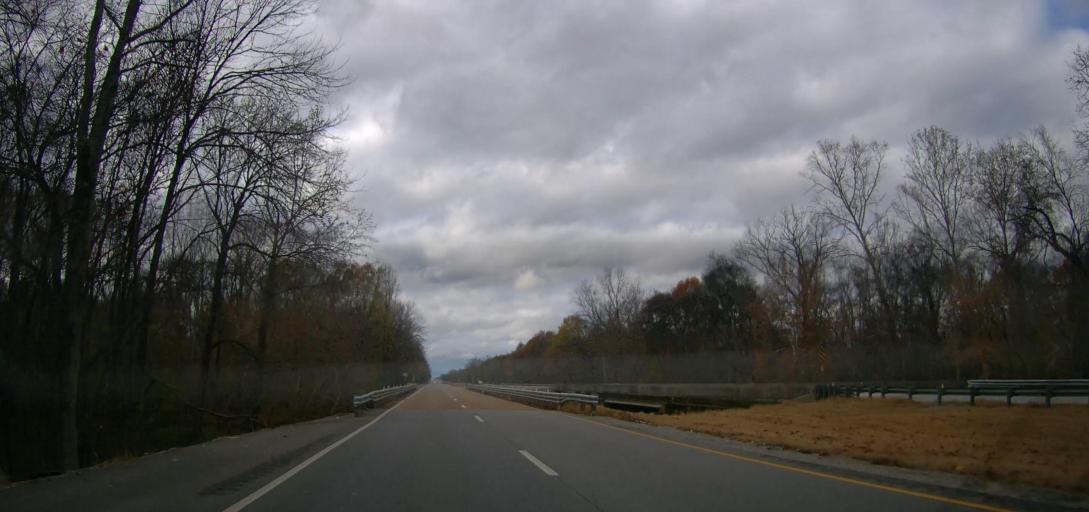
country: US
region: Alabama
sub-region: Lawrence County
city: Town Creek
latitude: 34.6312
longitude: -87.4858
